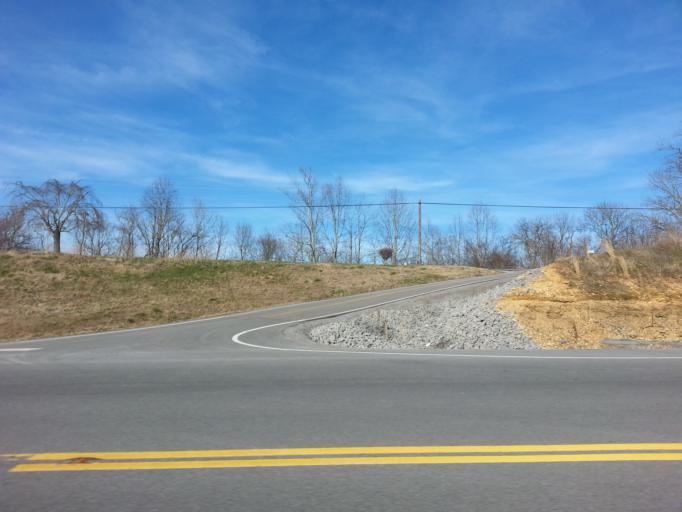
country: US
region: Tennessee
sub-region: Cannon County
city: Woodbury
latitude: 35.8000
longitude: -86.0002
